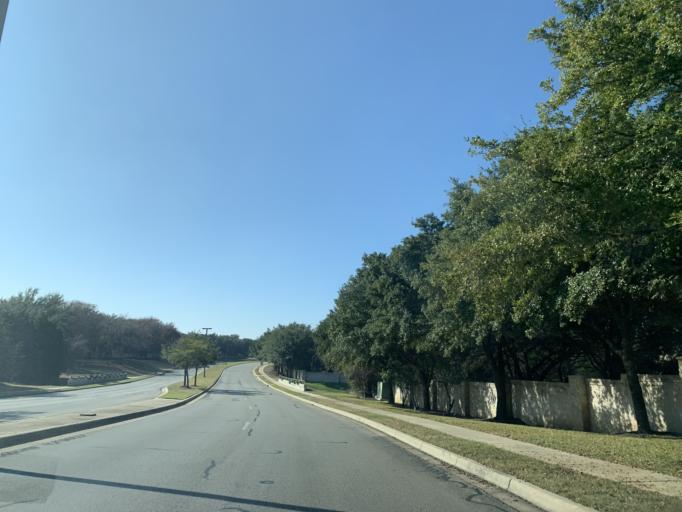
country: US
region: Texas
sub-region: Travis County
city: Windemere
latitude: 30.5082
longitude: -97.6206
